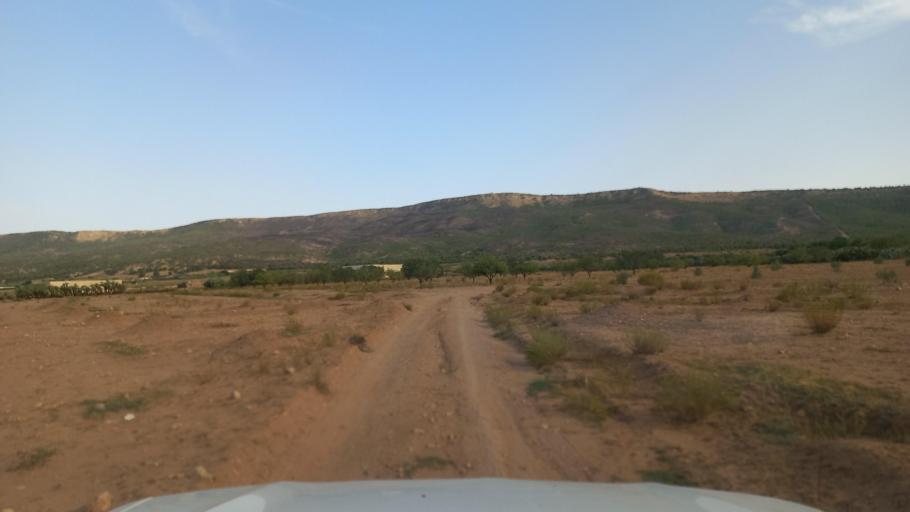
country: TN
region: Al Qasrayn
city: Kasserine
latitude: 35.3545
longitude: 8.8550
